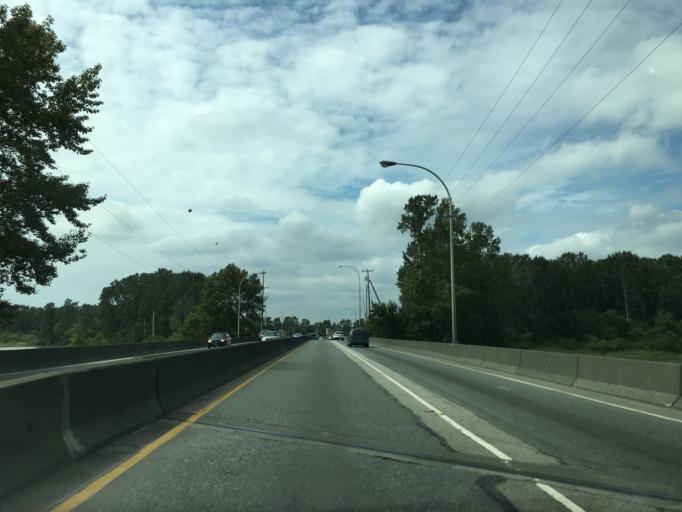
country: CA
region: British Columbia
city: Ladner
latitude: 49.1146
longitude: -123.0665
